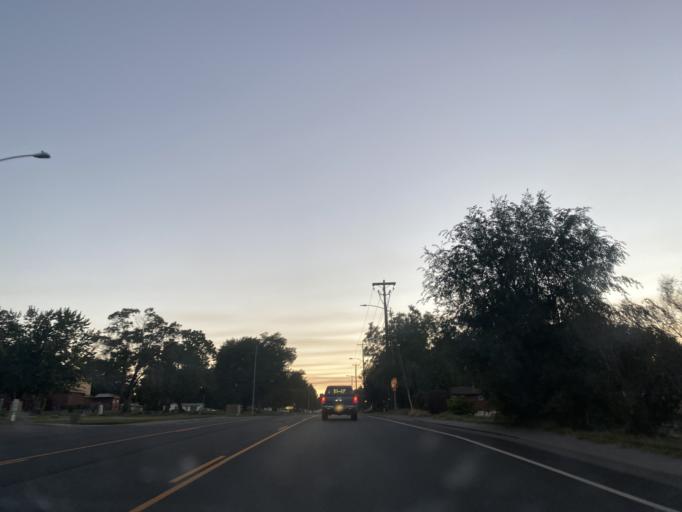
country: US
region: Washington
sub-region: Benton County
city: Kennewick
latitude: 46.1986
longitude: -119.1389
